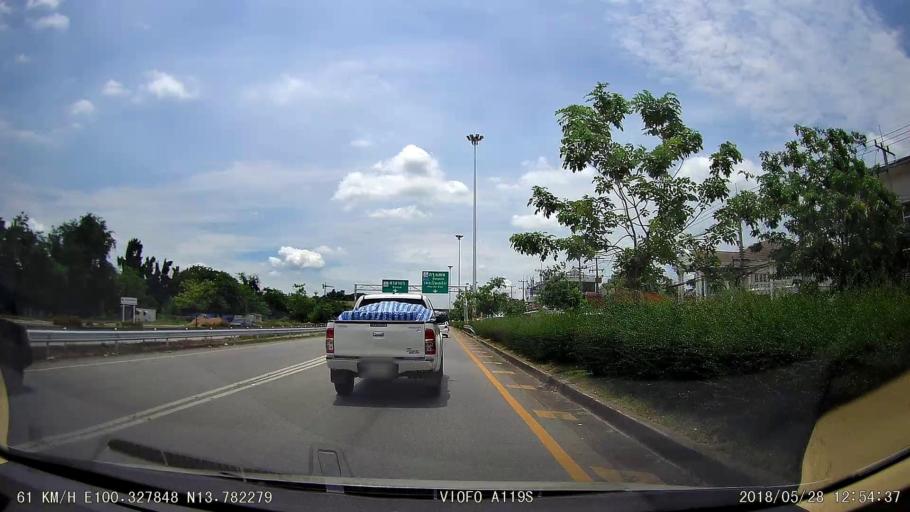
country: TH
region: Bangkok
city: Thawi Watthana
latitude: 13.7826
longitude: 100.3279
